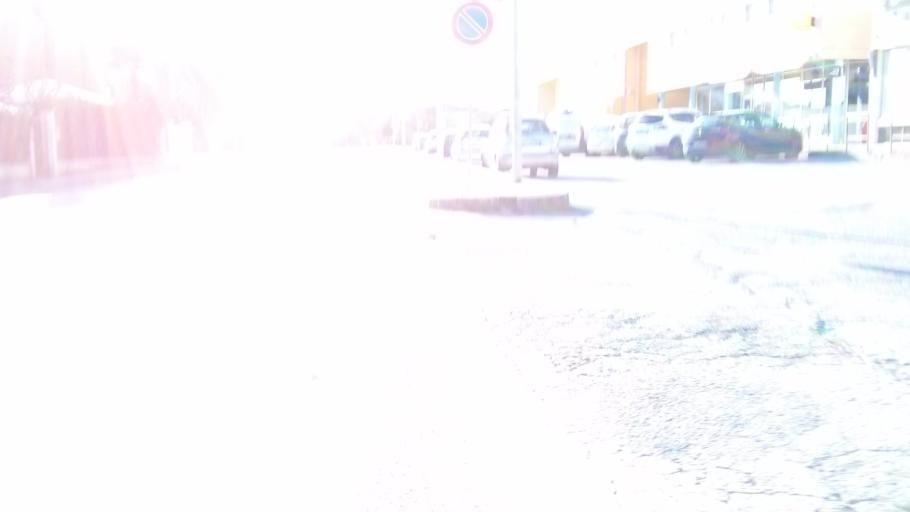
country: IT
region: The Marches
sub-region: Provincia di Pesaro e Urbino
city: Fano
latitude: 43.8362
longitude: 13.0298
